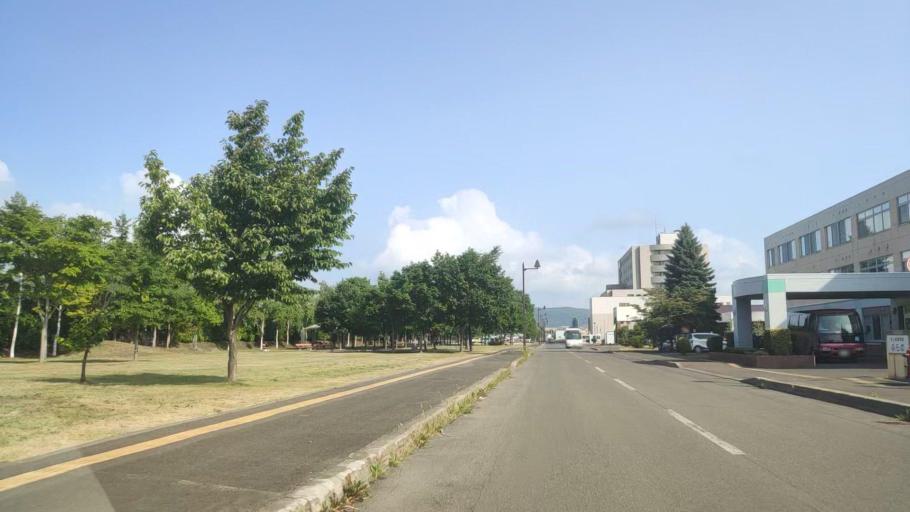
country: JP
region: Hokkaido
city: Shimo-furano
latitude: 43.3452
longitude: 142.3933
